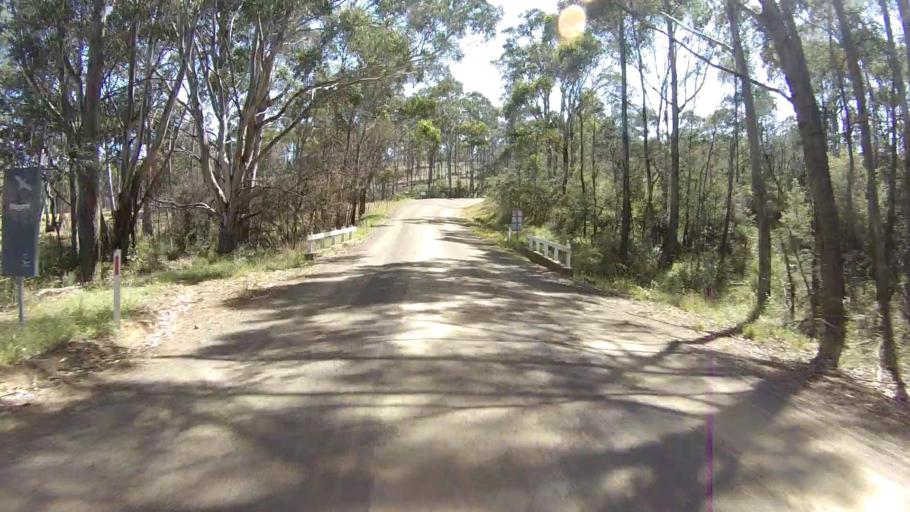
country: AU
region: Tasmania
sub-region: Sorell
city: Sorell
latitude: -42.7480
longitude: 147.7200
